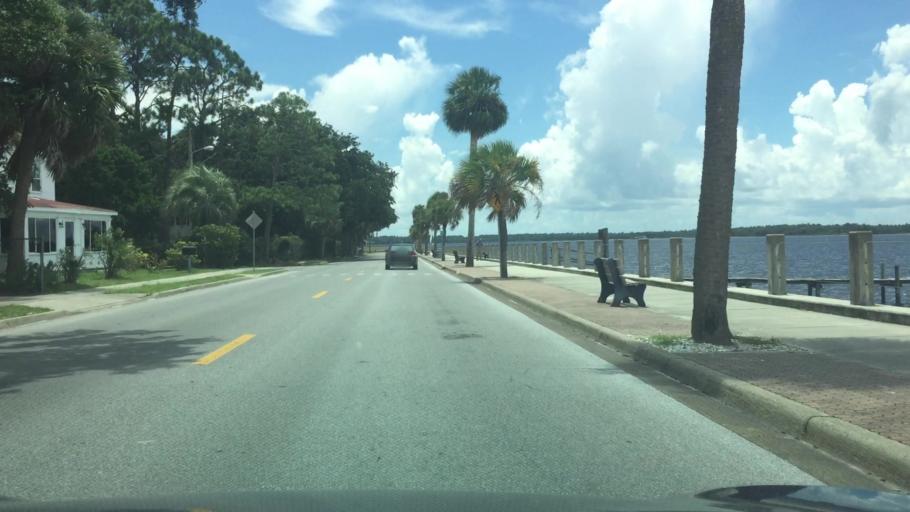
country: US
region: Florida
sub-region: Bay County
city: Panama City
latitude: 30.1482
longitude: -85.6587
